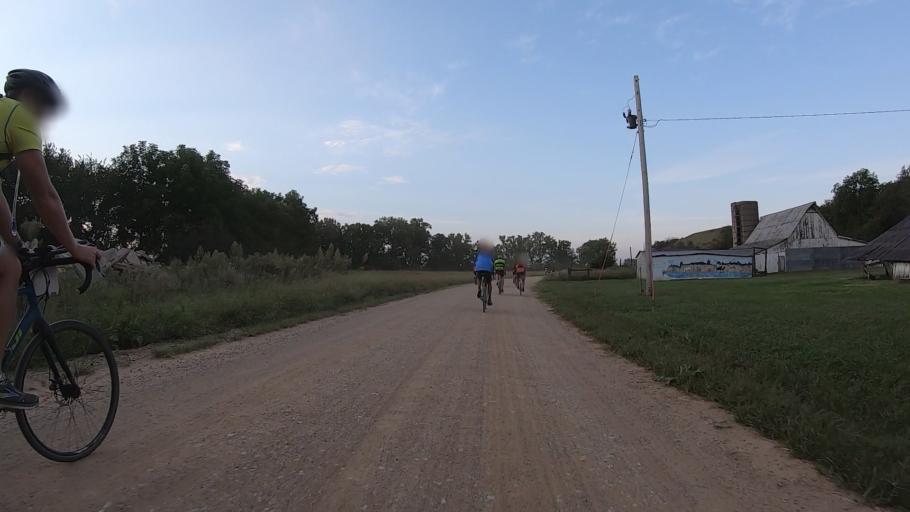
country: US
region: Kansas
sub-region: Marshall County
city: Marysville
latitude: 39.8313
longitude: -96.6647
